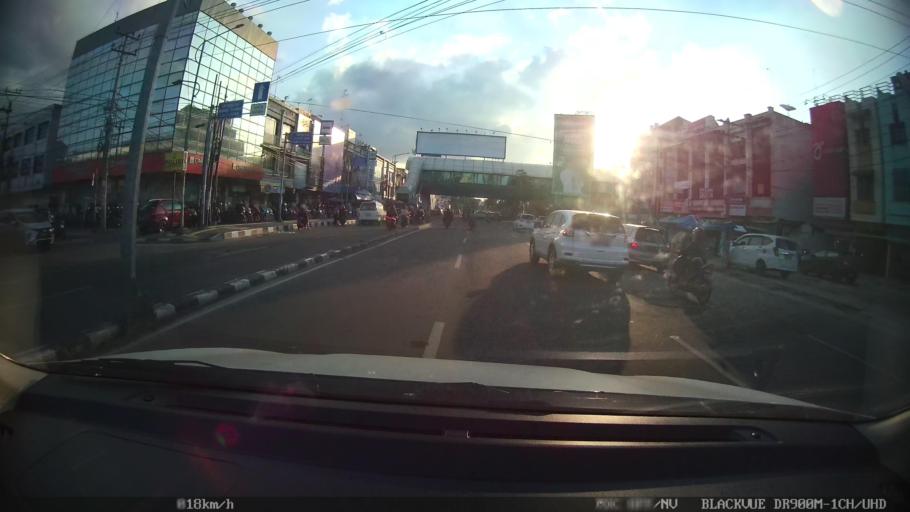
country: ID
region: North Sumatra
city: Medan
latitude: 3.5918
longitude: 98.6648
